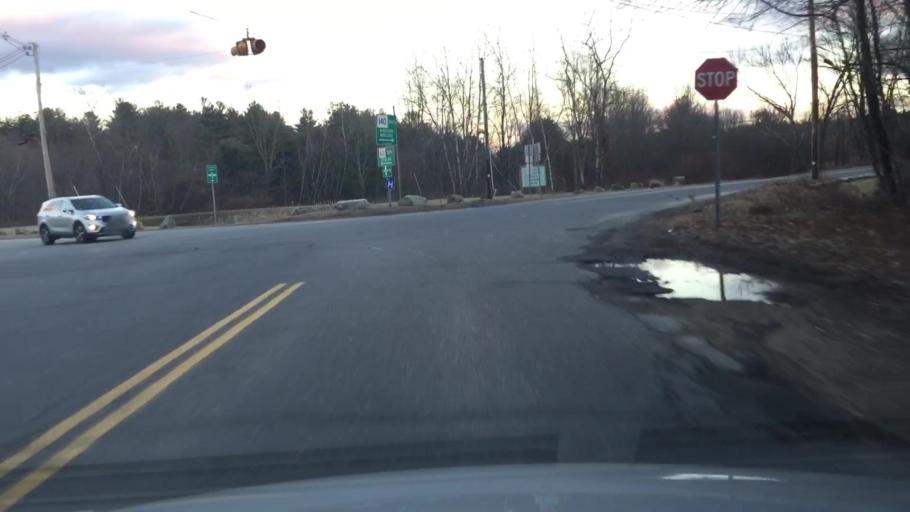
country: US
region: Massachusetts
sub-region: Worcester County
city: Sterling
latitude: 42.4334
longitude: -71.8125
